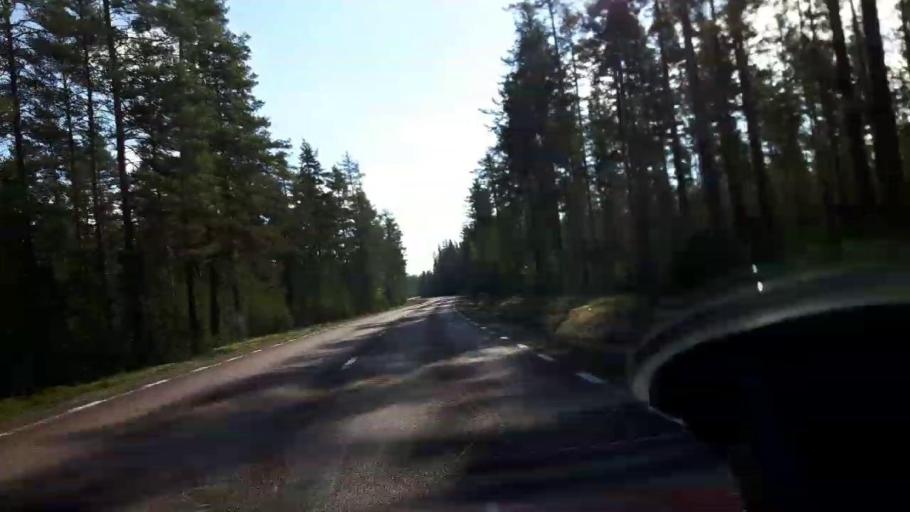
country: SE
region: Gaevleborg
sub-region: Ljusdals Kommun
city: Farila
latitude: 61.9191
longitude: 15.6139
